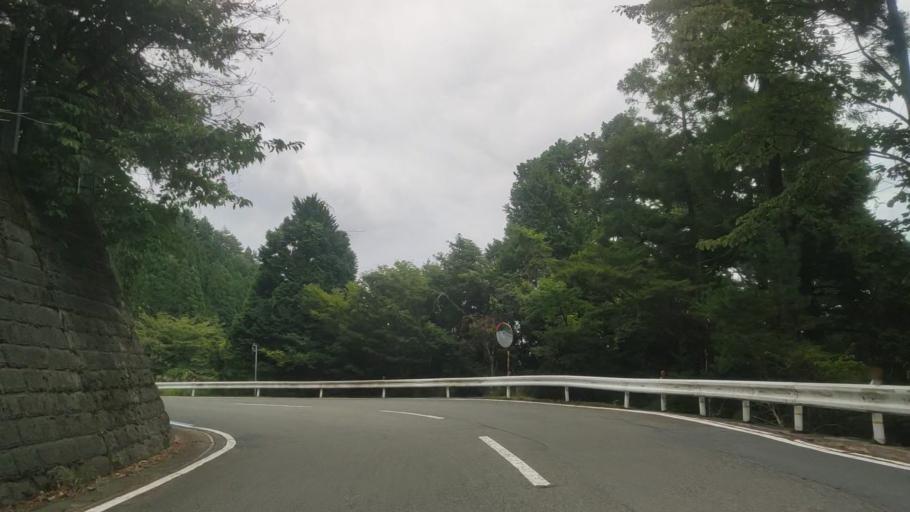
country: JP
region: Wakayama
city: Koya
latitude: 34.2202
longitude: 135.5614
